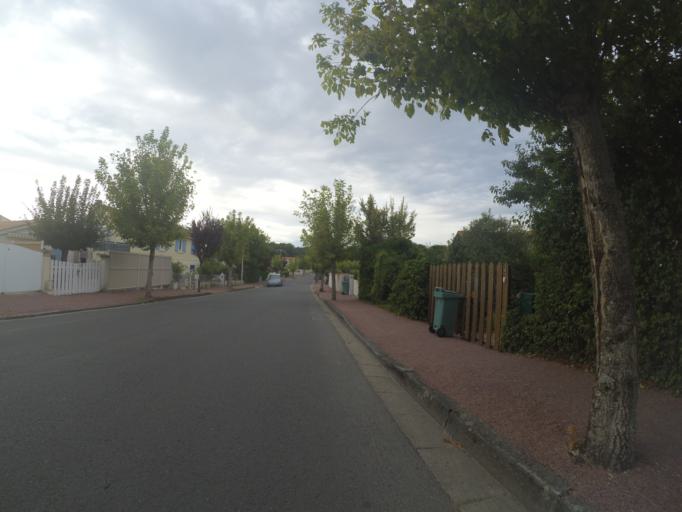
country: FR
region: Poitou-Charentes
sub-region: Departement de la Charente-Maritime
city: Meschers-sur-Gironde
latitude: 45.5627
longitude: -0.9592
